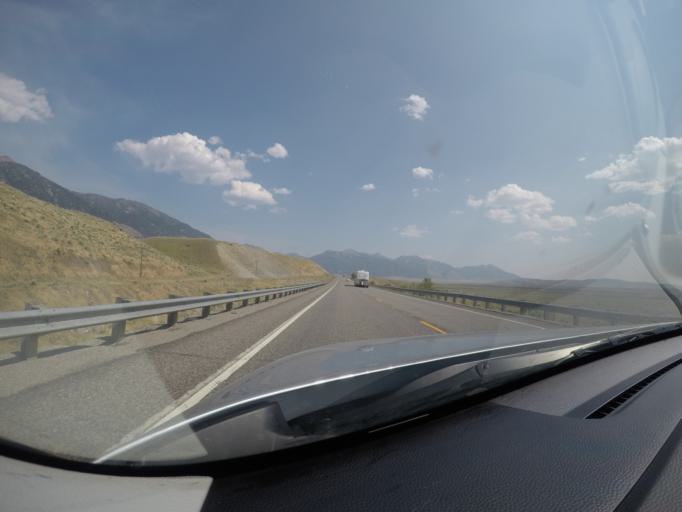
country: US
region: Montana
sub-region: Gallatin County
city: West Yellowstone
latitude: 44.8421
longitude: -111.5191
